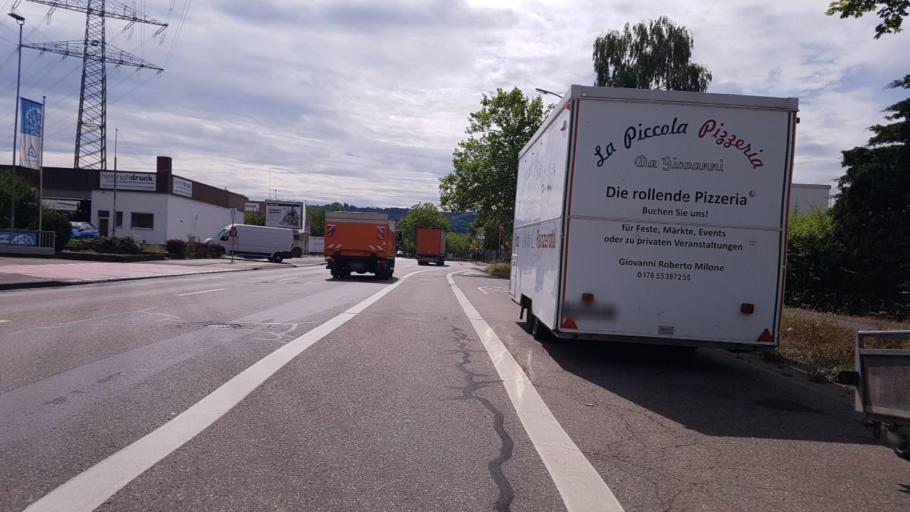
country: DE
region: Rheinland-Pfalz
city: Niederwerth
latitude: 50.3855
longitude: 7.5996
